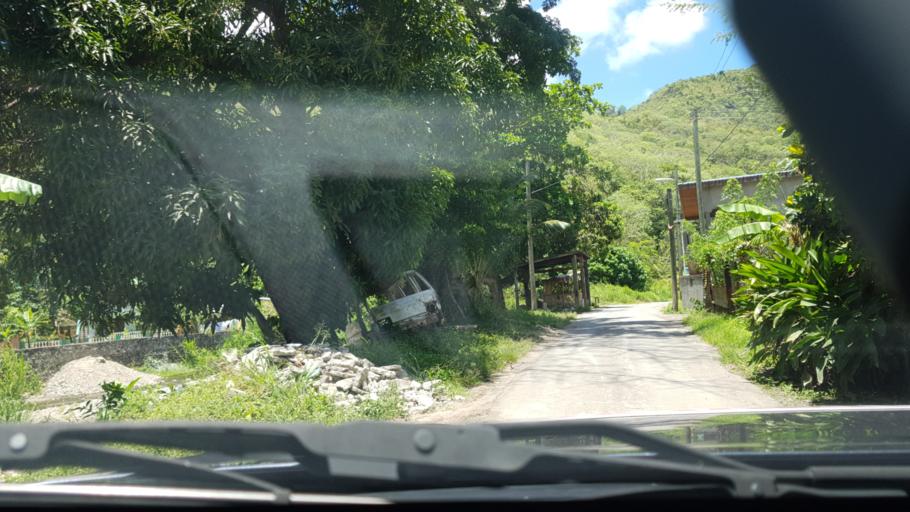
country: LC
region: Anse-la-Raye
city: Canaries
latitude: 13.9028
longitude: -61.0658
